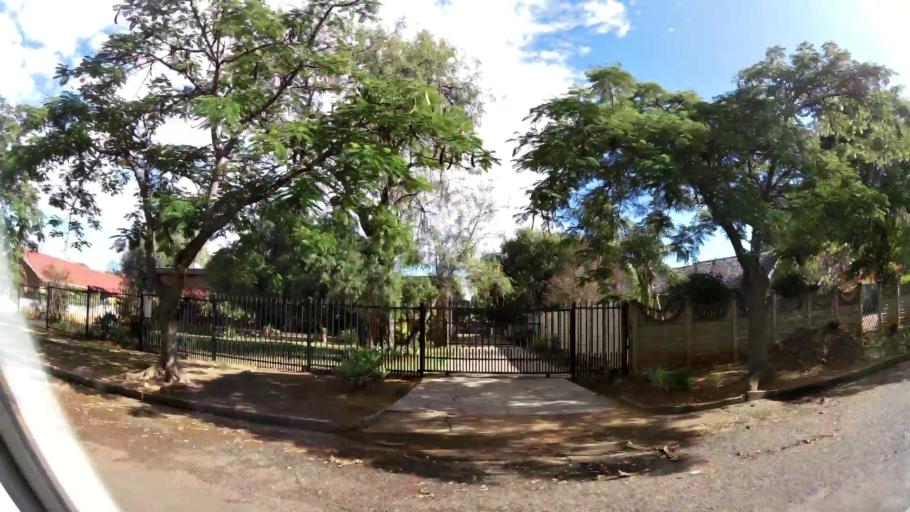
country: ZA
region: Limpopo
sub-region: Waterberg District Municipality
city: Warmbaths
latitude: -24.8768
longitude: 28.2883
